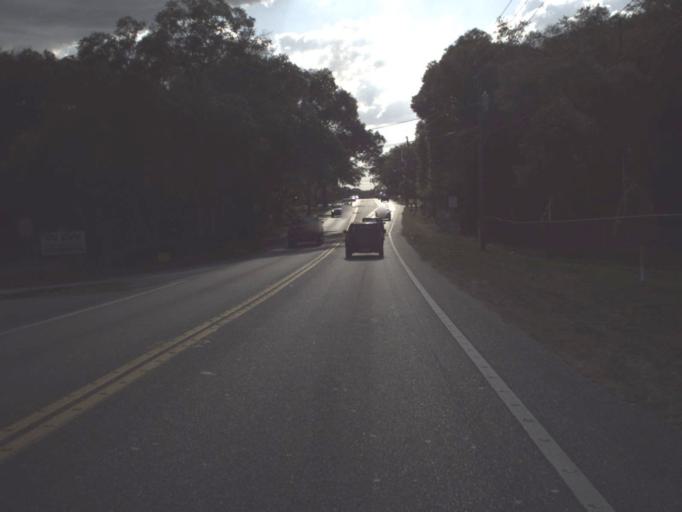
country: US
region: Florida
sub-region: Lake County
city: Mount Plymouth
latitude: 28.8078
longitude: -81.5549
